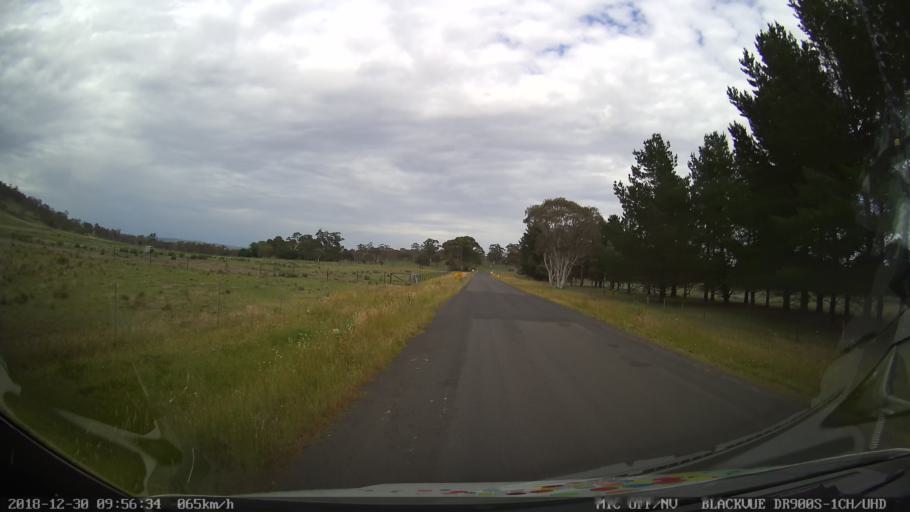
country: AU
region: New South Wales
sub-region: Cooma-Monaro
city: Cooma
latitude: -36.5229
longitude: 149.2502
